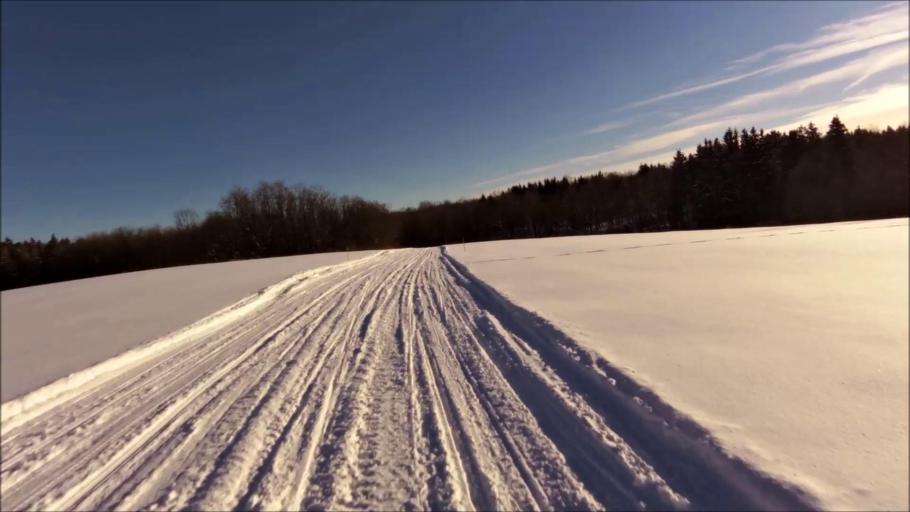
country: US
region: New York
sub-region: Chautauqua County
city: Mayville
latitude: 42.2513
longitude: -79.3859
